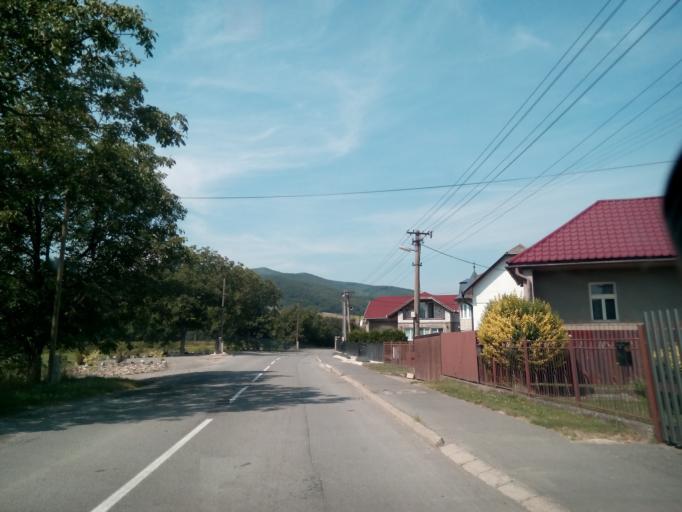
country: SK
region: Kosicky
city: Kosice
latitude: 48.8026
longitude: 21.2432
